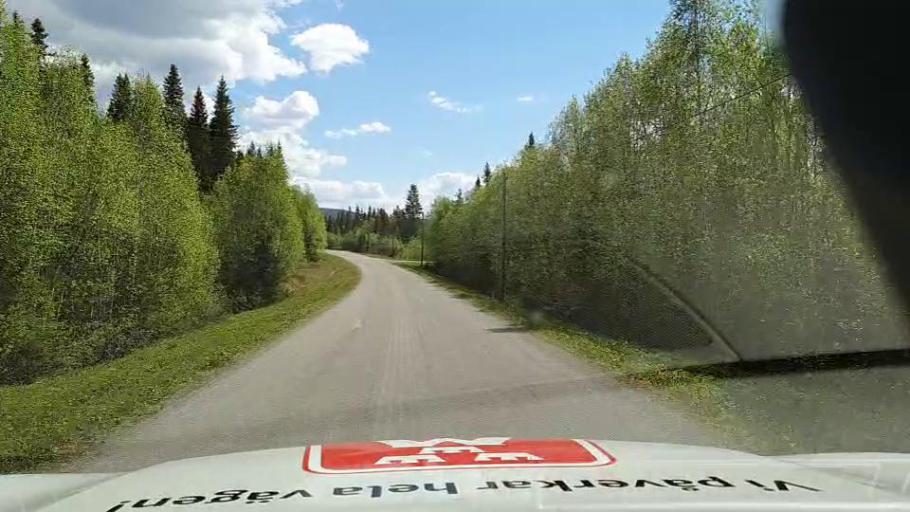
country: NO
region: Nord-Trondelag
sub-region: Lierne
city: Sandvika
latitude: 64.1295
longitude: 14.1216
